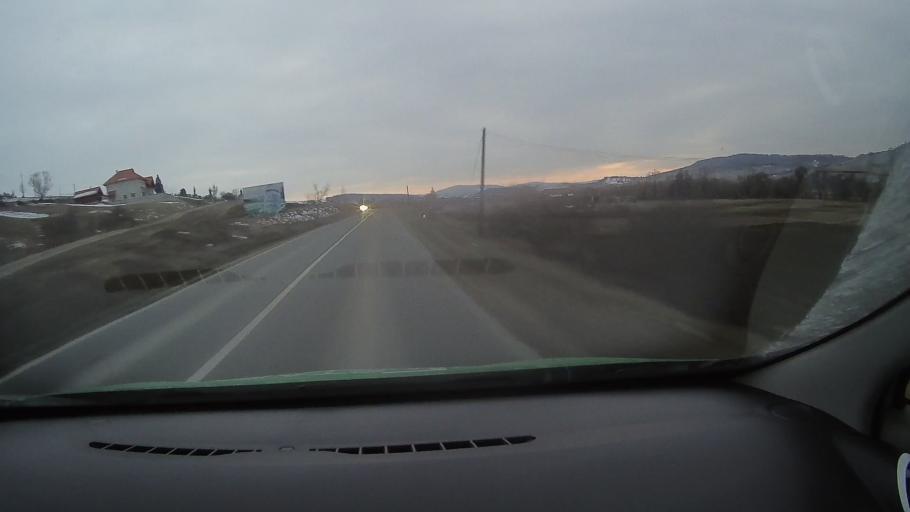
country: RO
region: Harghita
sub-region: Municipiul Odorheiu Secuiesc
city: Odorheiu Secuiesc
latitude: 46.2797
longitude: 25.2884
